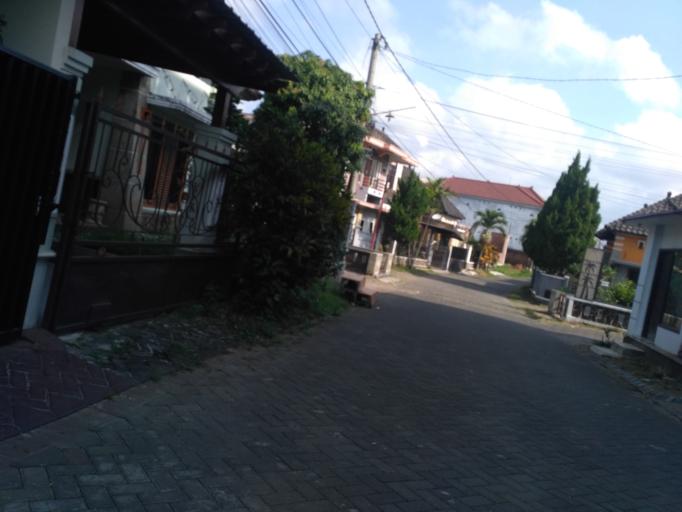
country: ID
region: East Java
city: Malang
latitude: -7.9360
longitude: 112.6140
